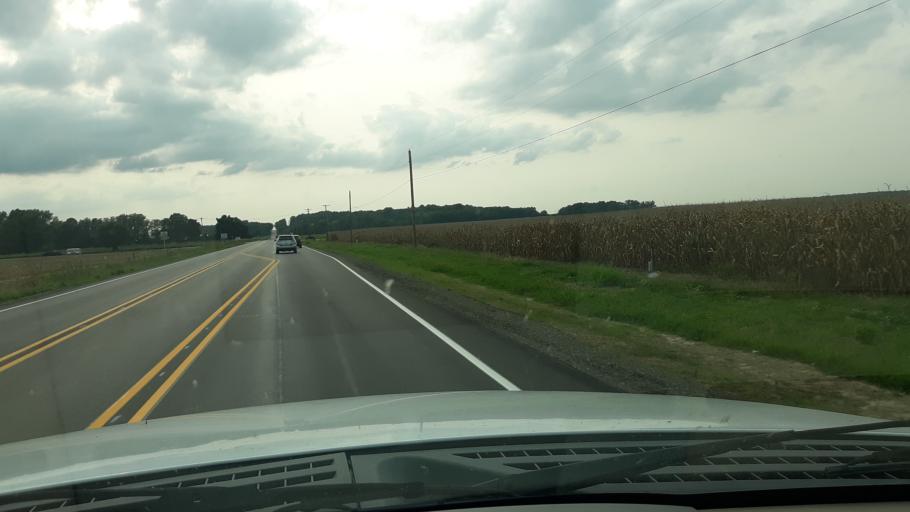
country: US
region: Indiana
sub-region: Gibson County
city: Princeton
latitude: 38.3558
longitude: -87.6376
